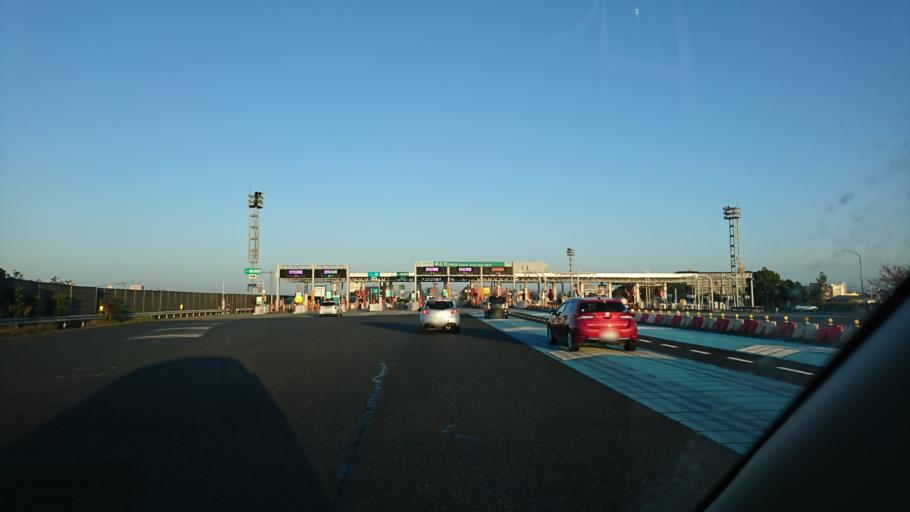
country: JP
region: Hyogo
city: Kakogawacho-honmachi
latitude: 34.7191
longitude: 134.8998
